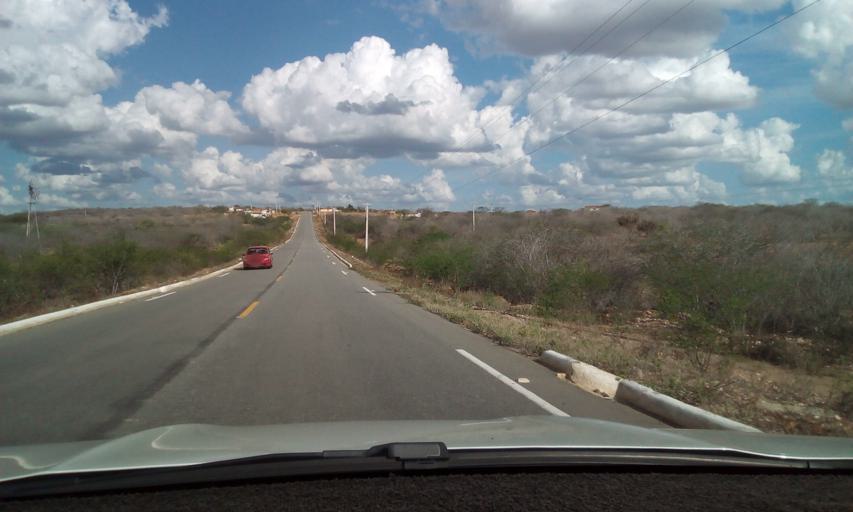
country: BR
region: Paraiba
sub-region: Soledade
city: Soledade
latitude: -6.7954
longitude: -36.4124
